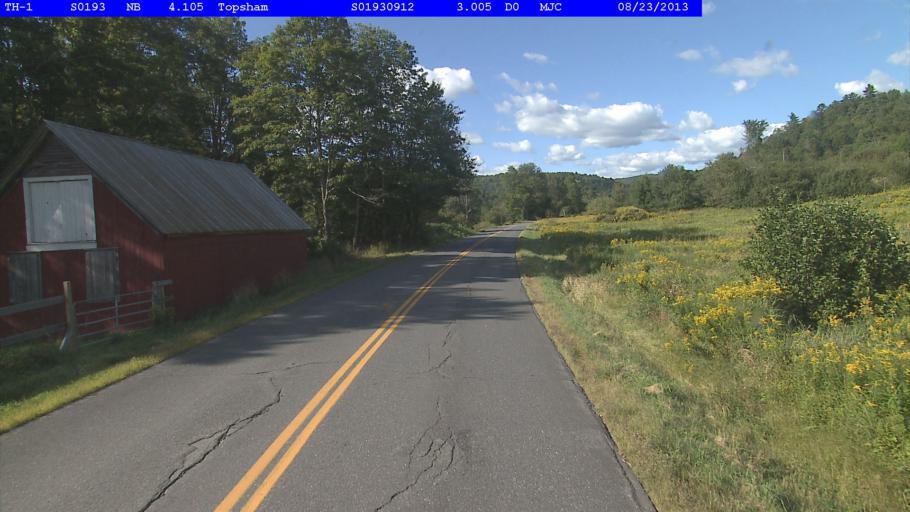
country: US
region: New Hampshire
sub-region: Grafton County
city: Haverhill
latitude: 44.1106
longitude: -72.2339
